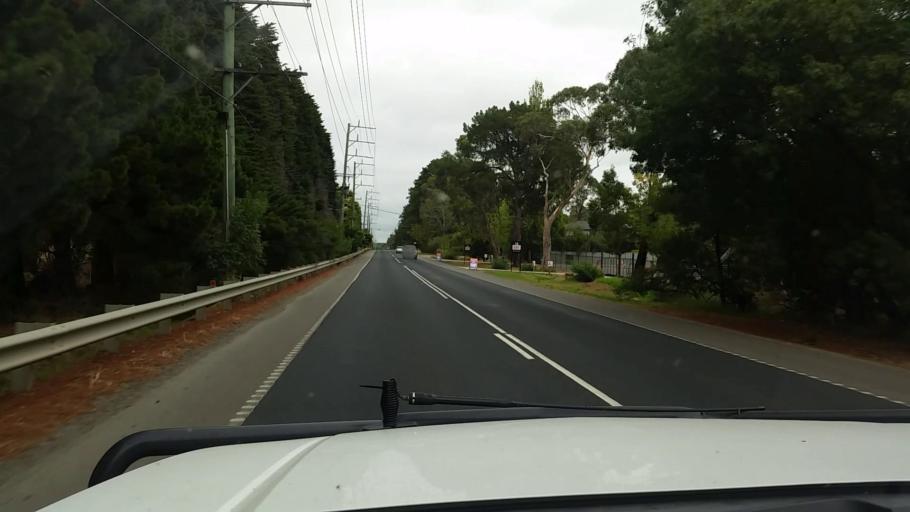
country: AU
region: Victoria
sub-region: Mornington Peninsula
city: Tyabb
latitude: -38.2662
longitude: 145.1979
